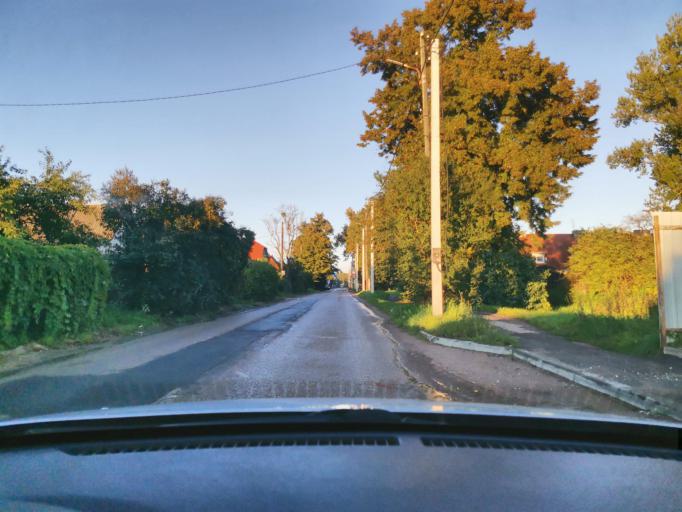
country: RU
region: Kaliningrad
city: Chernyakhovsk
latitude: 54.6594
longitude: 21.8336
